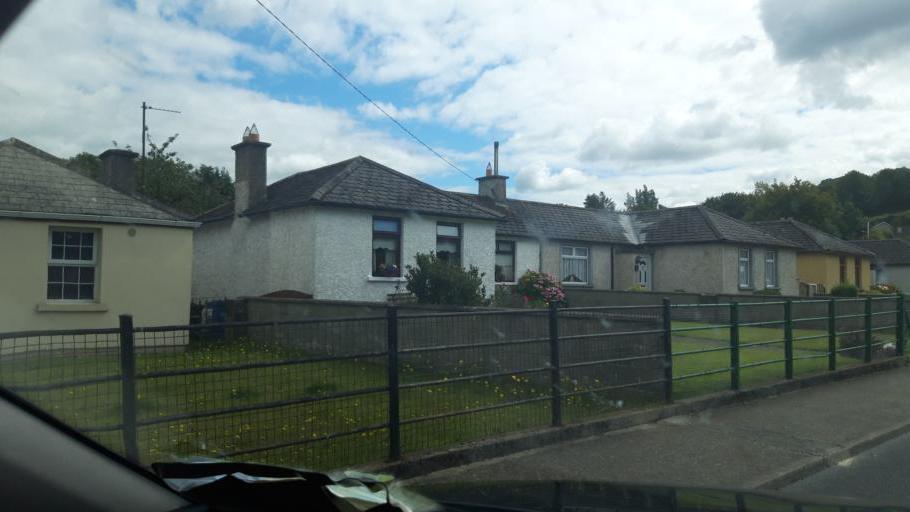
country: IE
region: Munster
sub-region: South Tipperary
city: Cluain Meala
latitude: 52.3483
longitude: -7.7038
